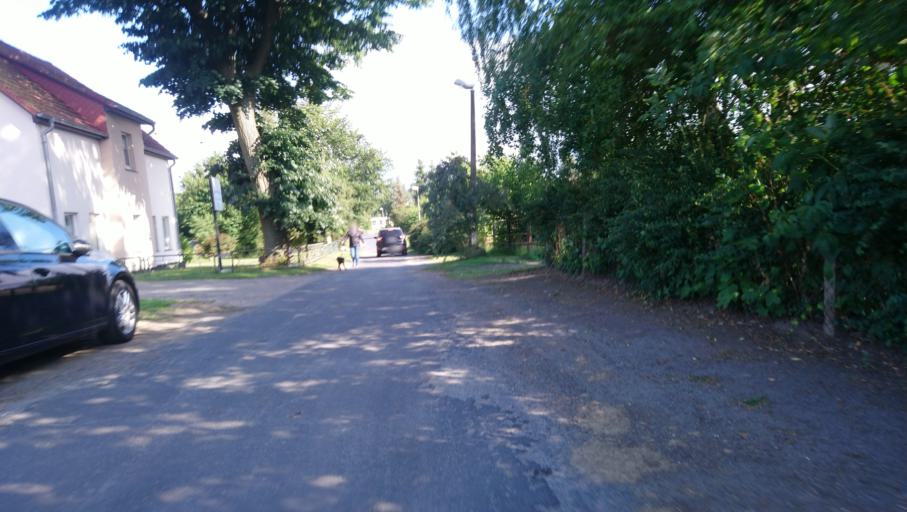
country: DE
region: Mecklenburg-Vorpommern
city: Papendorf
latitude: 54.0662
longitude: 12.1002
